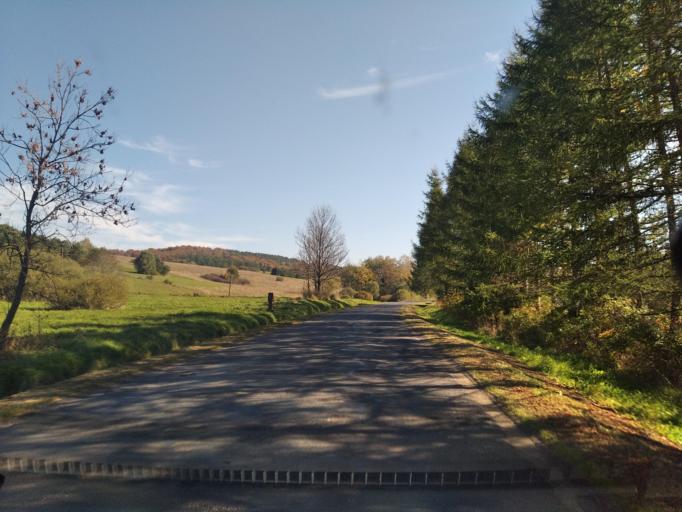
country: PL
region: Subcarpathian Voivodeship
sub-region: Powiat sanocki
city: Bukowsko
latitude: 49.4140
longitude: 21.9736
